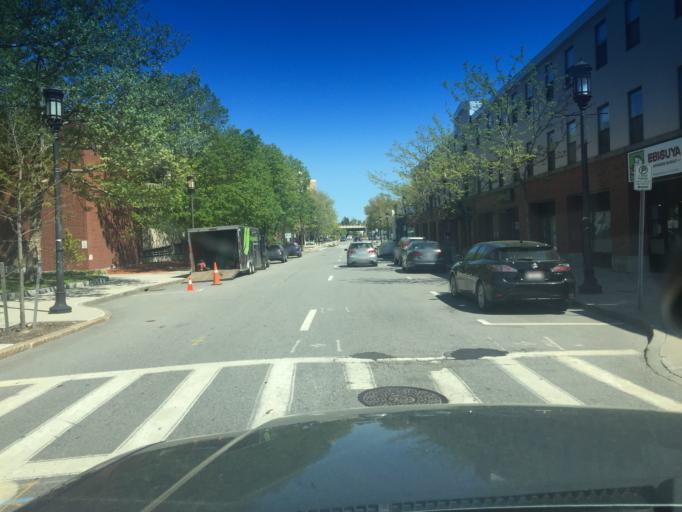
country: US
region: Massachusetts
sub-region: Middlesex County
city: Medford
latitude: 42.4177
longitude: -71.1079
